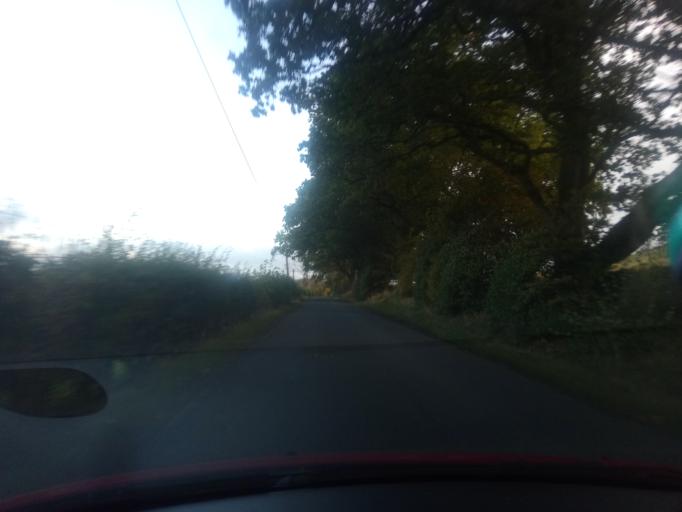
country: GB
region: Scotland
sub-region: The Scottish Borders
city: Hawick
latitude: 55.3676
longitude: -2.6509
